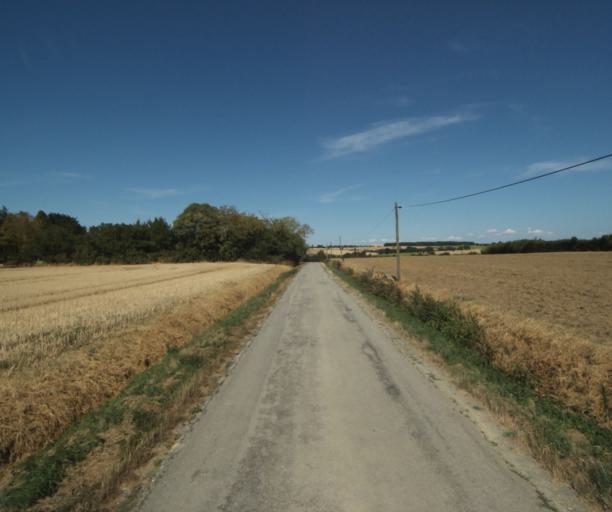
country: FR
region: Midi-Pyrenees
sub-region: Departement de la Haute-Garonne
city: Saint-Felix-Lauragais
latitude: 43.4945
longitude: 1.9026
